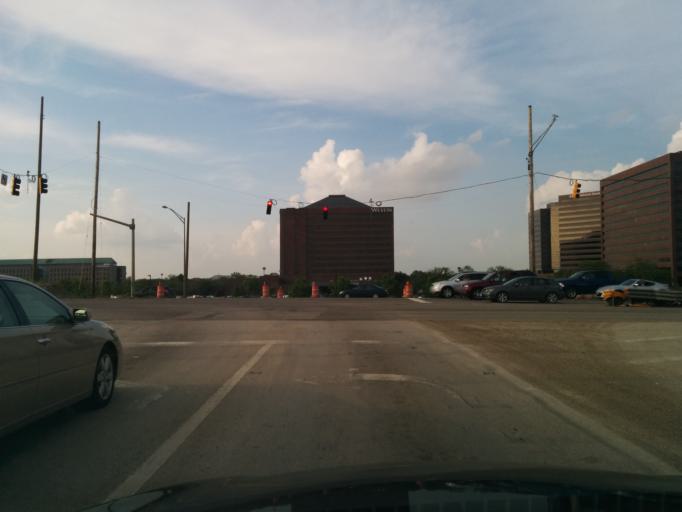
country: US
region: Illinois
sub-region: DuPage County
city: Itasca
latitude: 41.9846
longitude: -88.0206
